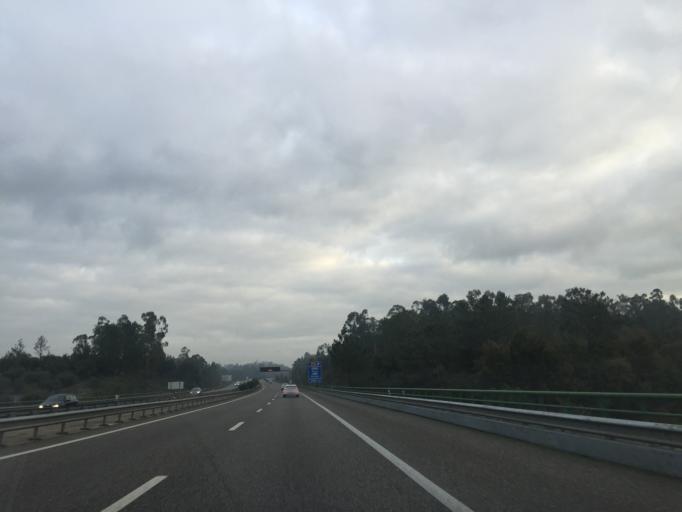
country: PT
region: Coimbra
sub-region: Soure
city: Soure
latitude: 40.0257
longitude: -8.5893
